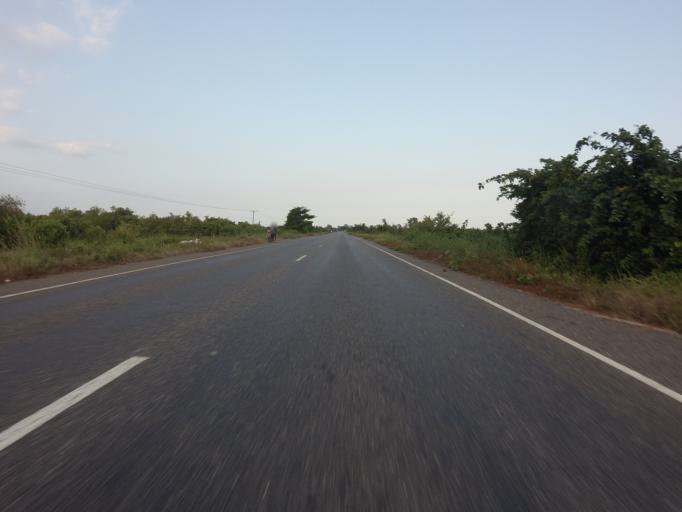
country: GH
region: Volta
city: Anloga
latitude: 6.0768
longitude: 0.5972
